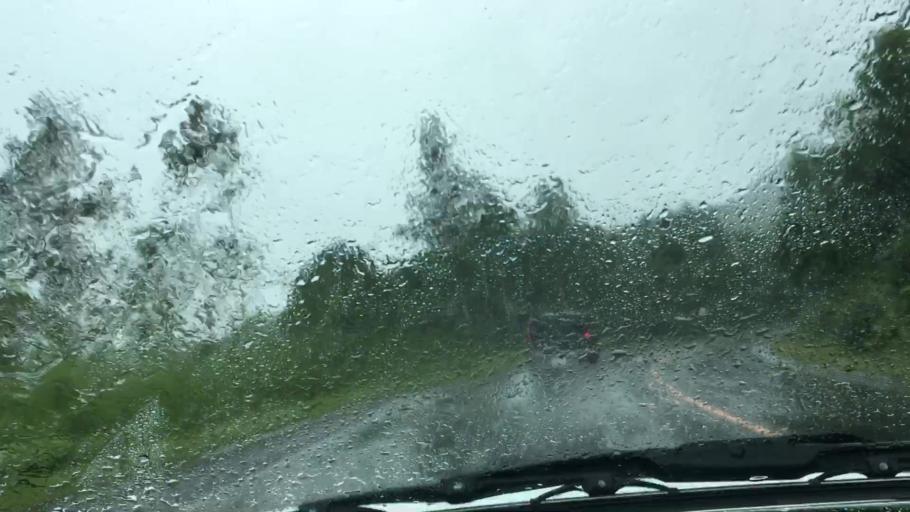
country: JP
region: Hokkaido
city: Sapporo
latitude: 42.8860
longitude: 141.1417
